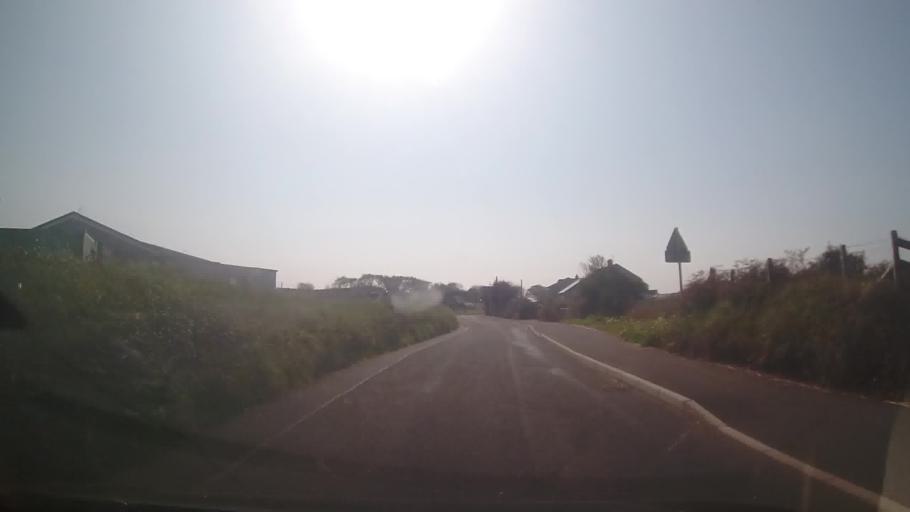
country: GB
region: Wales
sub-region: Pembrokeshire
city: Saint David's
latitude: 51.8868
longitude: -5.2596
